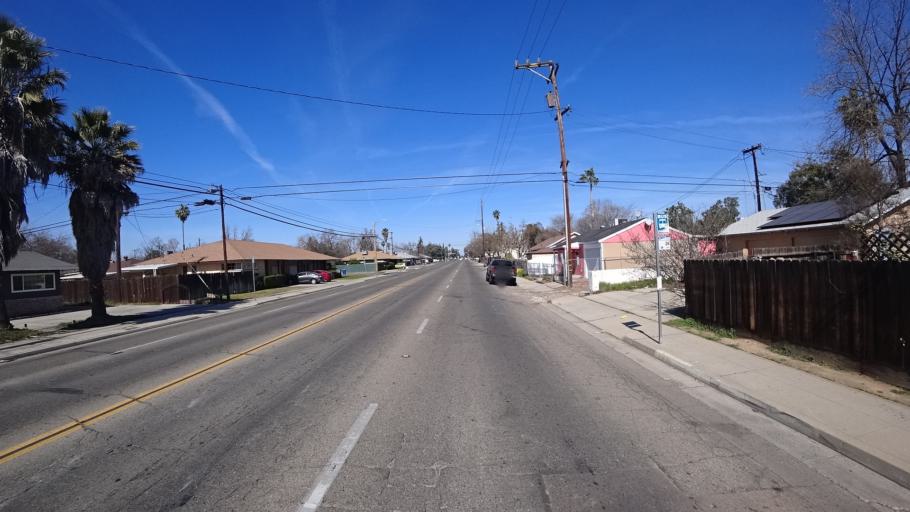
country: US
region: California
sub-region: Fresno County
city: Fresno
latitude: 36.7832
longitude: -119.8086
